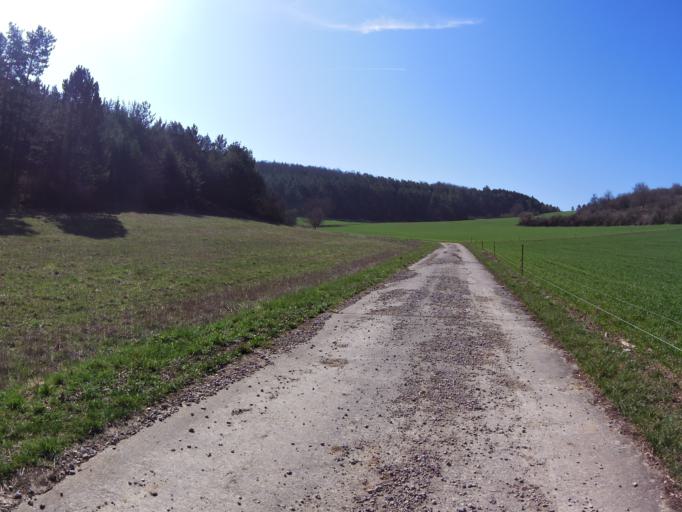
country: DE
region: Bavaria
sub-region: Regierungsbezirk Unterfranken
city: Erlabrunn
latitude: 49.8540
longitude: 9.8176
